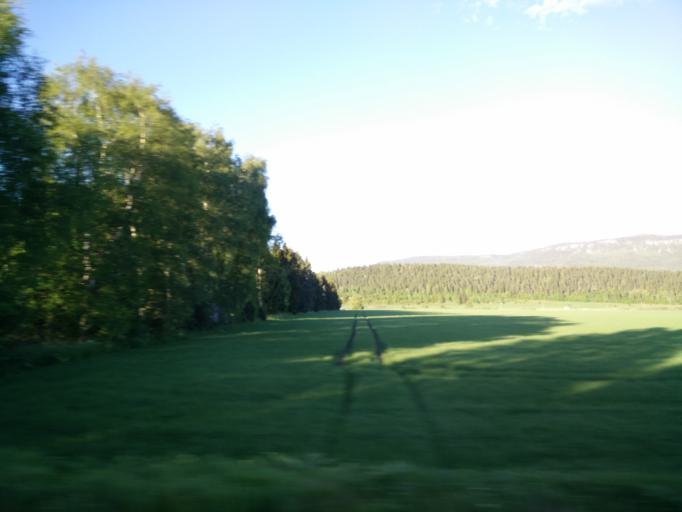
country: NO
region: Buskerud
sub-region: Hole
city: Vik
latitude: 60.1072
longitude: 10.2868
